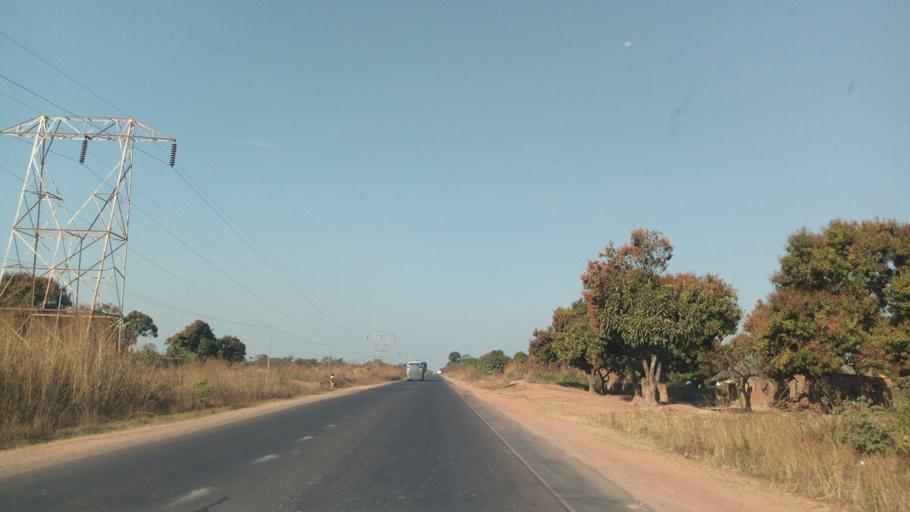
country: CD
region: Katanga
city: Likasi
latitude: -11.0021
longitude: 26.8590
